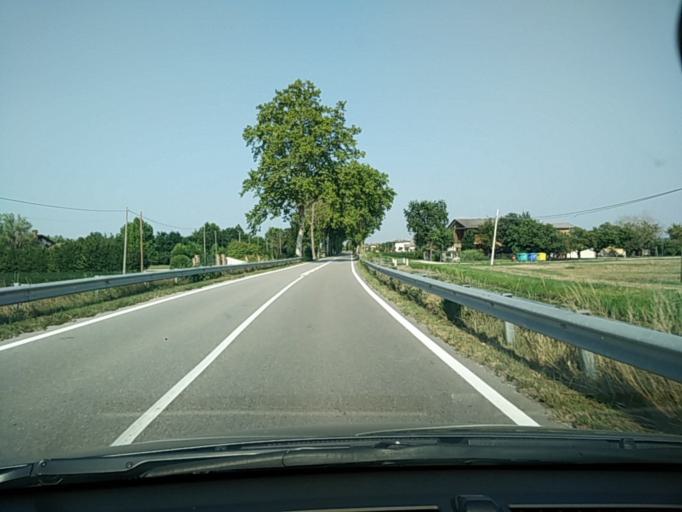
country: IT
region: Veneto
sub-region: Provincia di Venezia
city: Crepaldo
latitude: 45.6040
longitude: 12.7023
